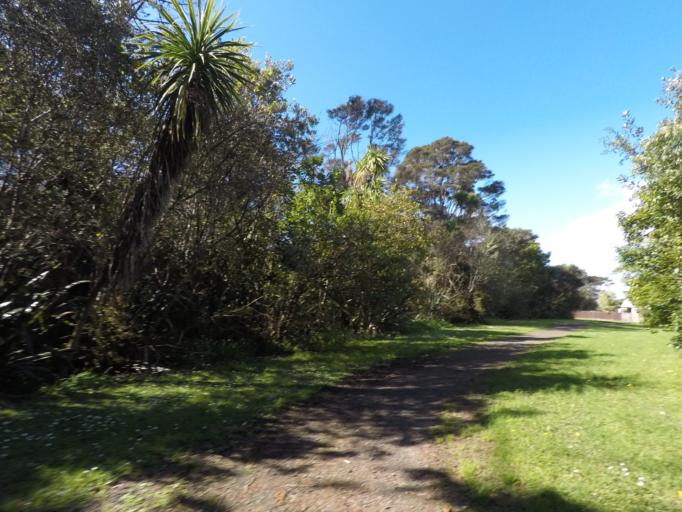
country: NZ
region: Auckland
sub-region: Auckland
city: Rosebank
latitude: -36.8603
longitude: 174.5953
